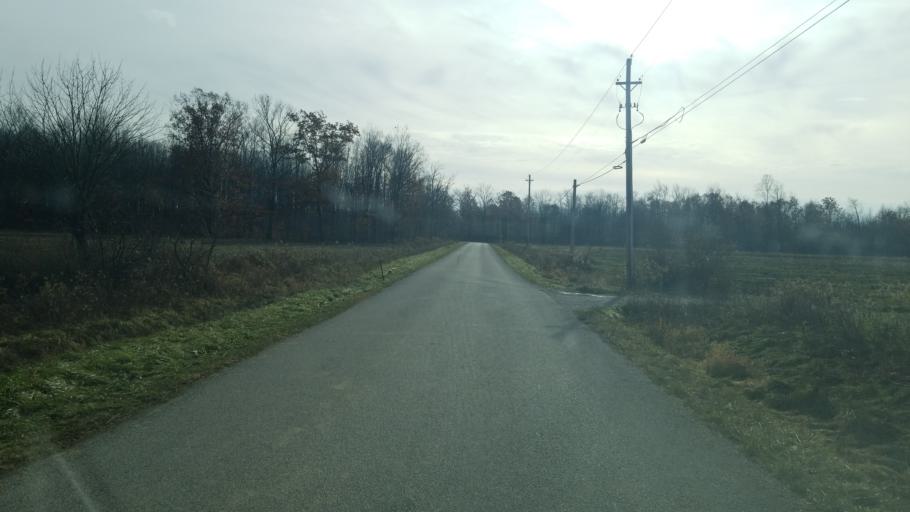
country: US
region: Ohio
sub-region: Ashtabula County
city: Roaming Shores
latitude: 41.6687
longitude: -80.9247
